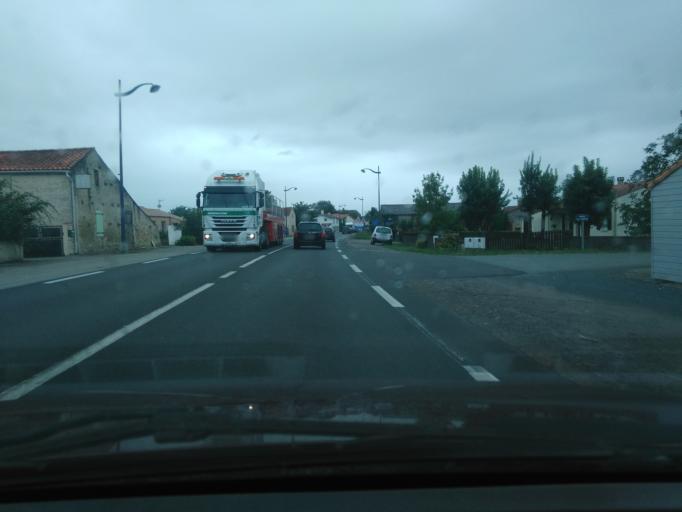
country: FR
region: Pays de la Loire
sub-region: Departement de la Vendee
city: Sainte-Gemme-la-Plaine
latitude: 46.4777
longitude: -1.1119
